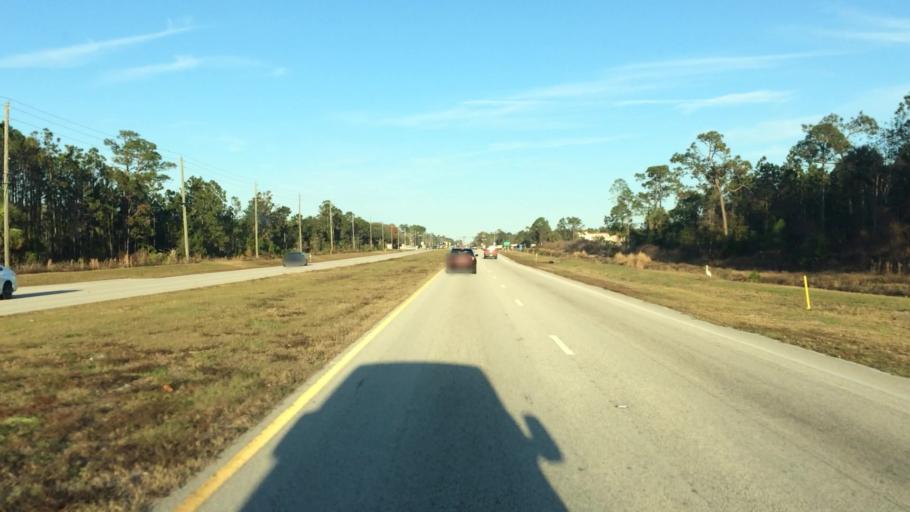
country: US
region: Florida
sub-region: Volusia County
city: Holly Hill
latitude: 29.2251
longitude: -81.0909
